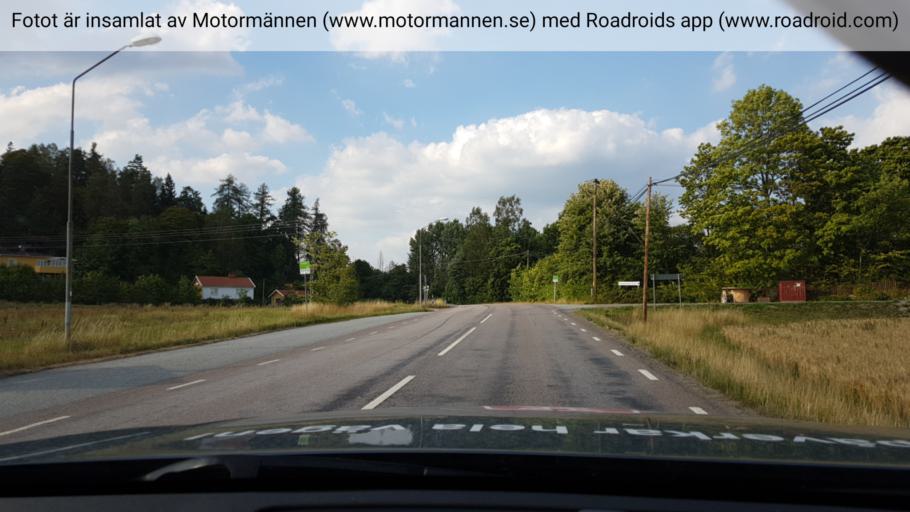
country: SE
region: Soedermanland
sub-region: Gnesta Kommun
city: Gnesta
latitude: 59.0577
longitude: 17.3048
